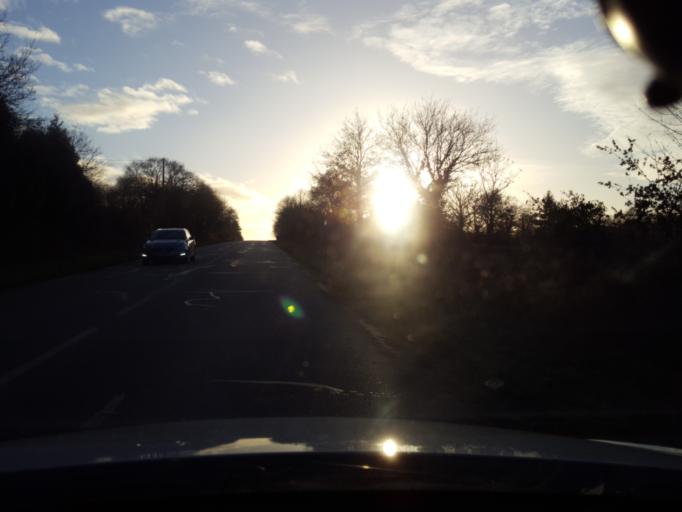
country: FR
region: Brittany
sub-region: Departement d'Ille-et-Vilaine
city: Guignen
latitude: 47.9357
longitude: -1.8442
